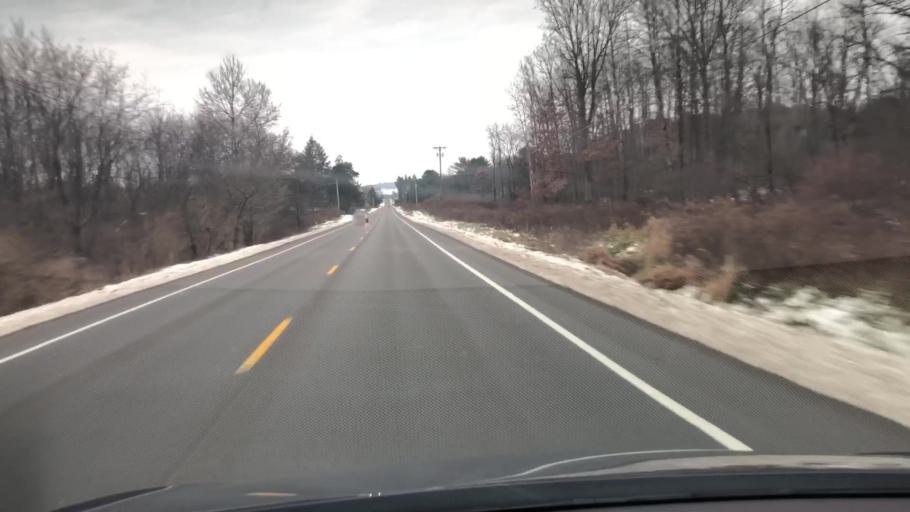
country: US
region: Pennsylvania
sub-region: Jefferson County
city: Brookville
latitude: 41.0888
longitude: -79.2282
